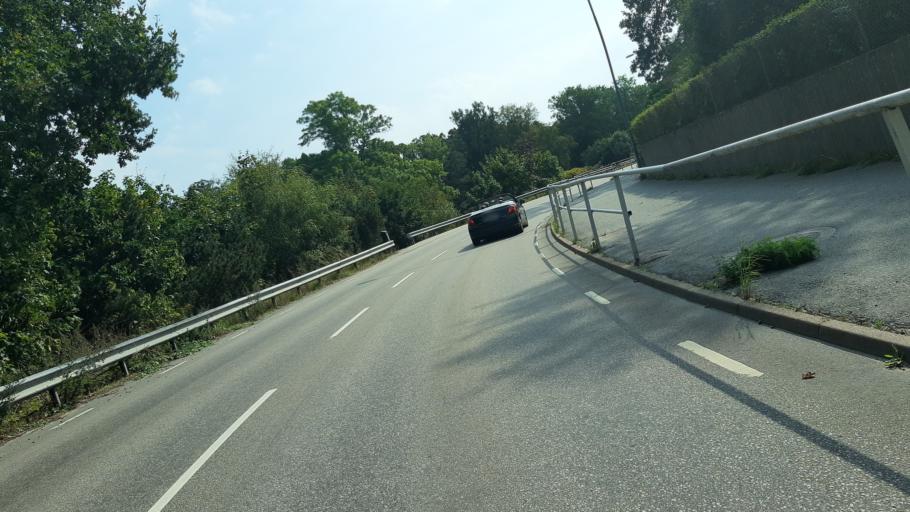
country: SE
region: Blekinge
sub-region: Karlskrona Kommun
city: Nattraby
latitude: 56.2055
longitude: 15.5335
